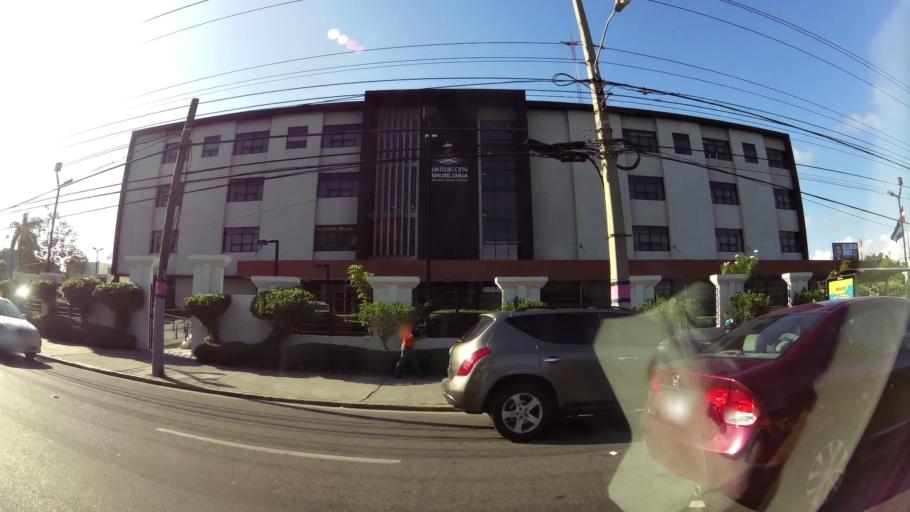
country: DO
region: Nacional
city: La Julia
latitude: 18.4507
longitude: -69.9283
